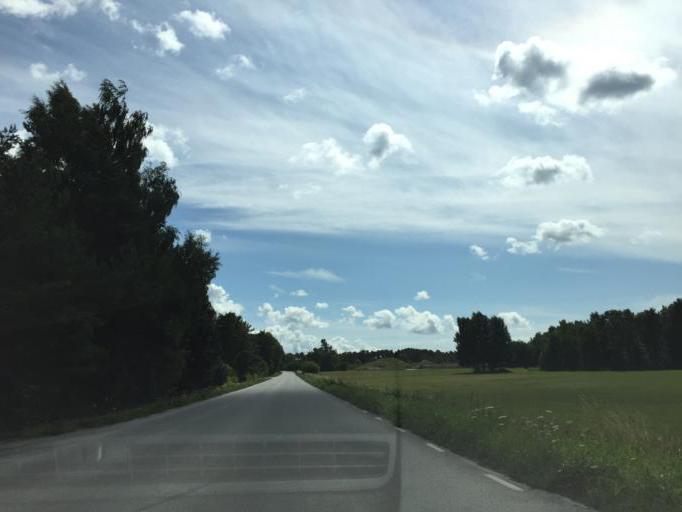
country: SE
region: Gotland
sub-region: Gotland
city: Visby
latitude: 57.6107
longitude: 18.2842
